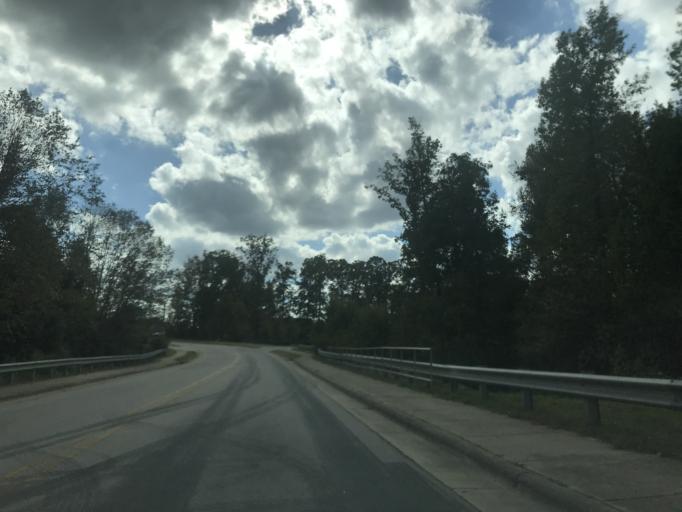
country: US
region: North Carolina
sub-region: Wake County
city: Garner
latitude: 35.7219
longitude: -78.6628
